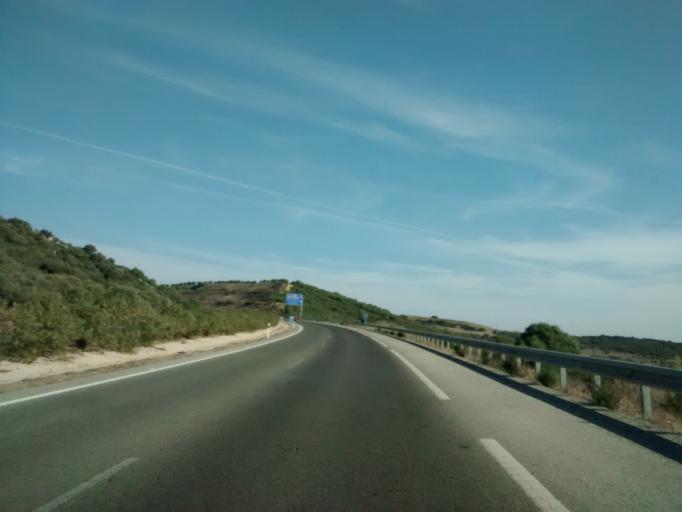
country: ES
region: Andalusia
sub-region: Provincia de Cadiz
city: Conil de la Frontera
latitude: 36.3375
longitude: -6.0488
